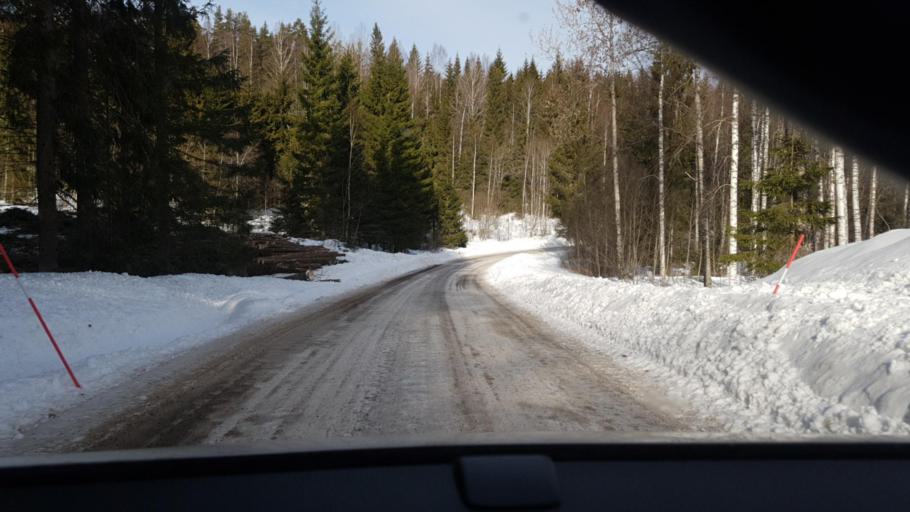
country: NO
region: Hedmark
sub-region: Eidskog
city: Skotterud
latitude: 59.8785
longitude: 11.9775
